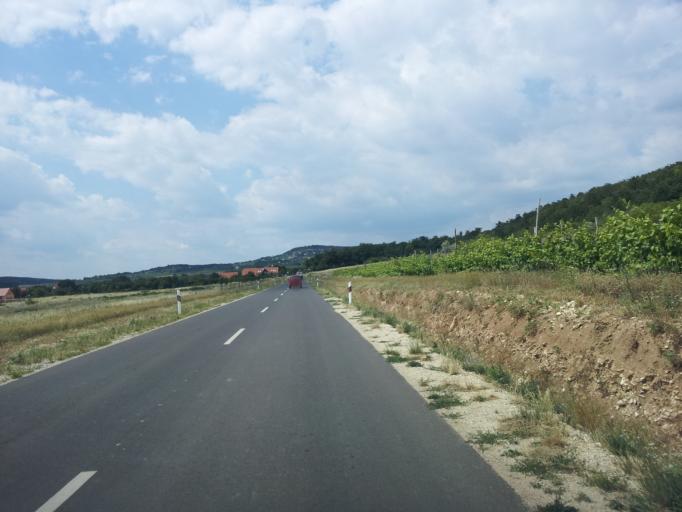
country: HU
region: Veszprem
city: Zanka
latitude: 46.9092
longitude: 17.7297
